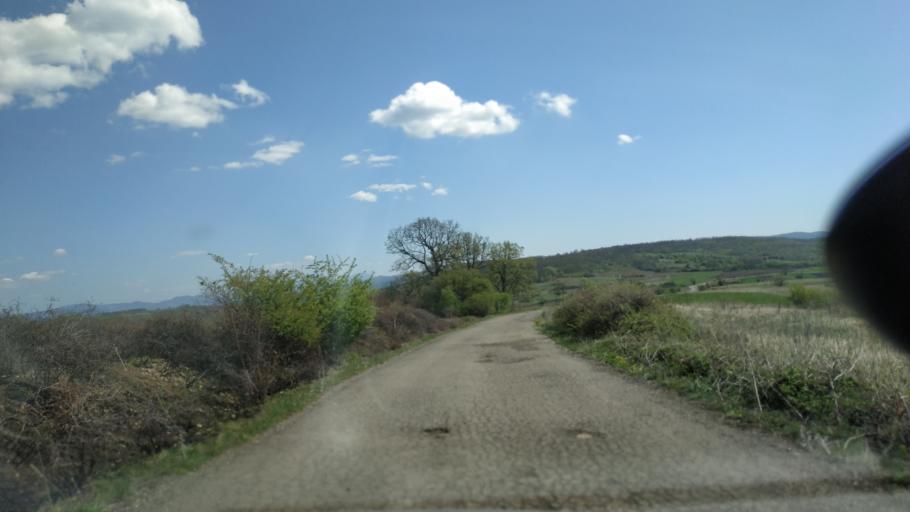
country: RS
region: Central Serbia
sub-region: Zajecarski Okrug
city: Soko Banja
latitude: 43.5206
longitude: 21.9058
